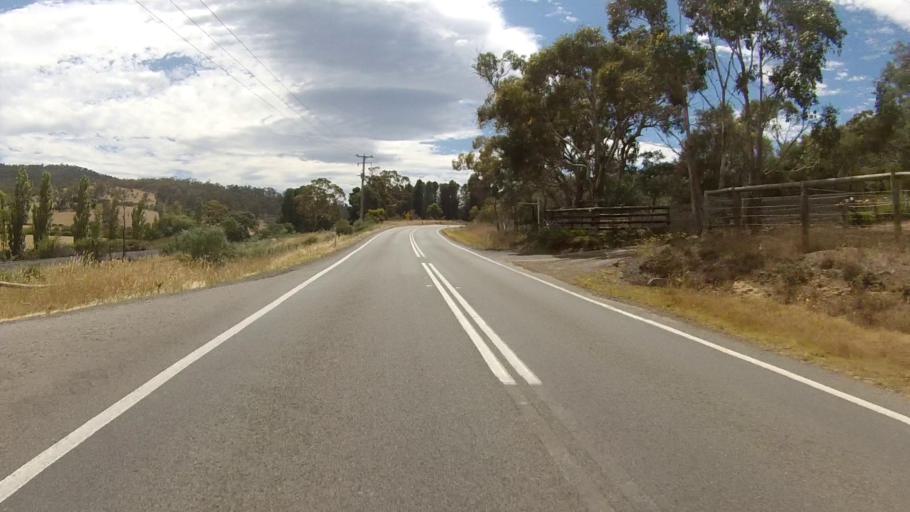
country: AU
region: Tasmania
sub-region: Brighton
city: Old Beach
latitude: -42.6725
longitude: 147.3614
